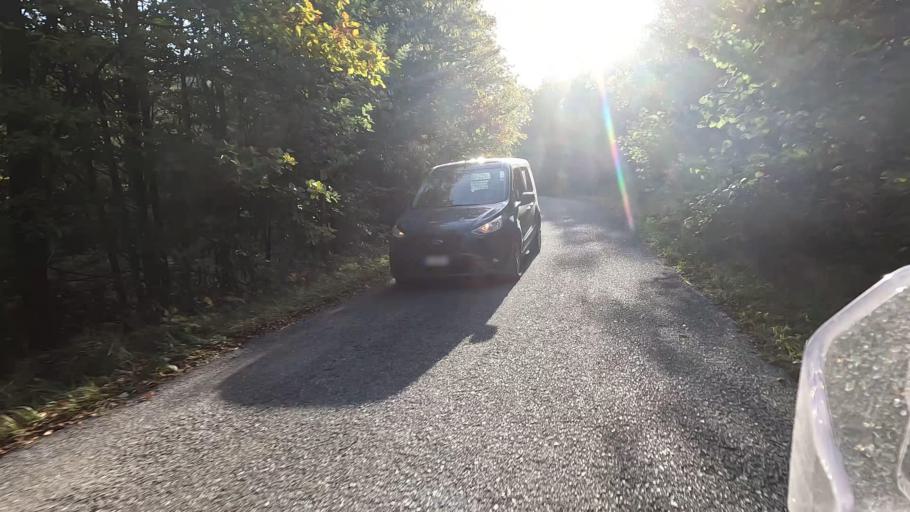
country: IT
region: Liguria
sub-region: Provincia di Savona
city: Urbe
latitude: 44.4437
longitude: 8.5784
